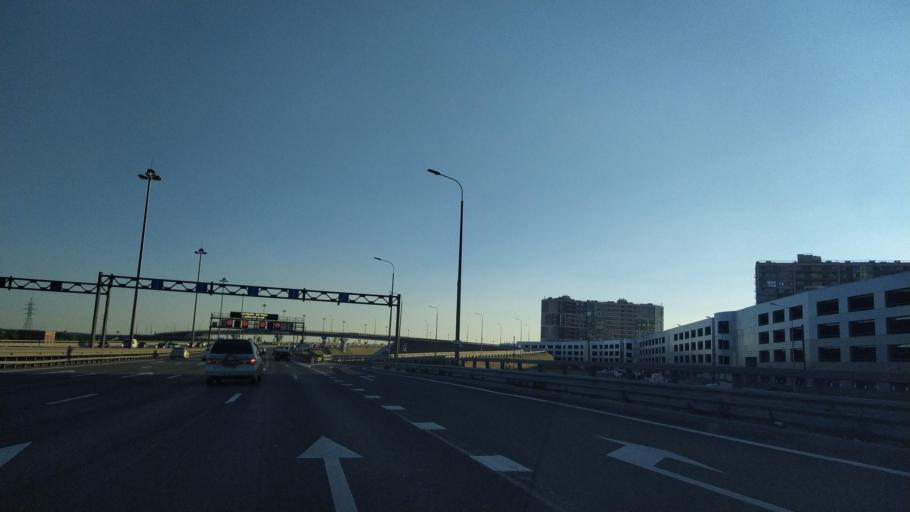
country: RU
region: St.-Petersburg
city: Shushary
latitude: 59.8135
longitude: 30.3456
